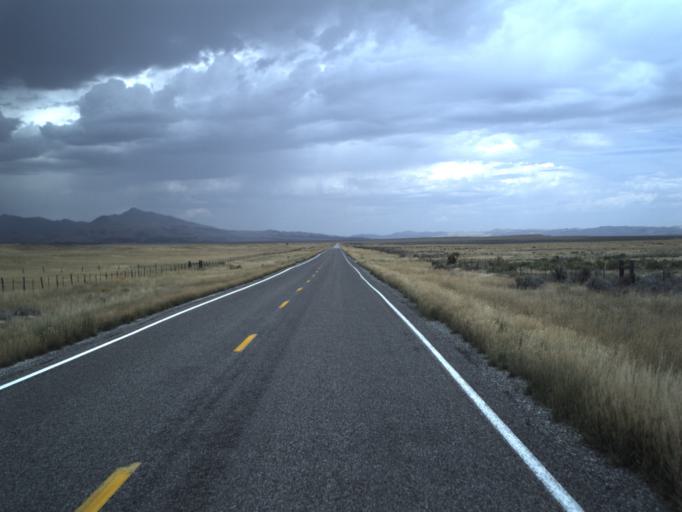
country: US
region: Idaho
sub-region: Oneida County
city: Malad City
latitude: 41.9122
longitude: -113.0999
